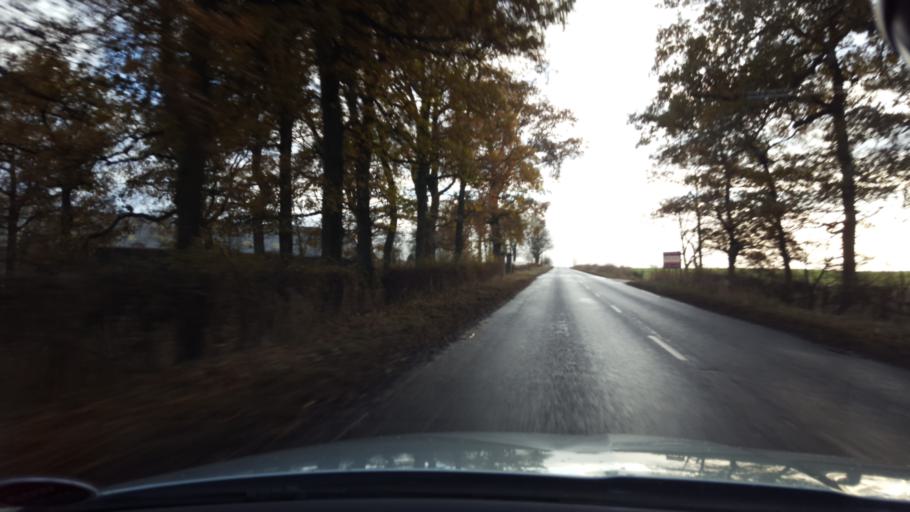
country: GB
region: Scotland
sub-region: Perth and Kinross
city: Milnathort
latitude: 56.2529
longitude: -3.3741
